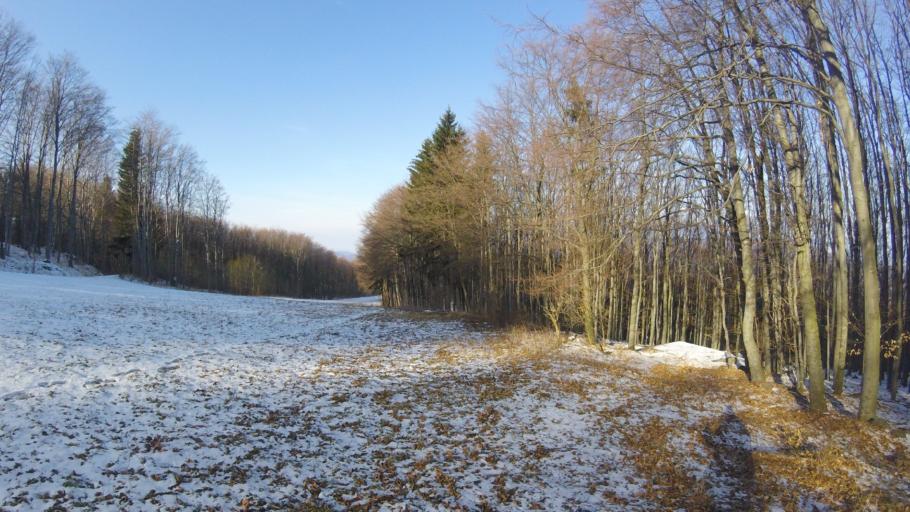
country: HU
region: Heves
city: Paradsasvar
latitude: 47.8725
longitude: 19.9924
